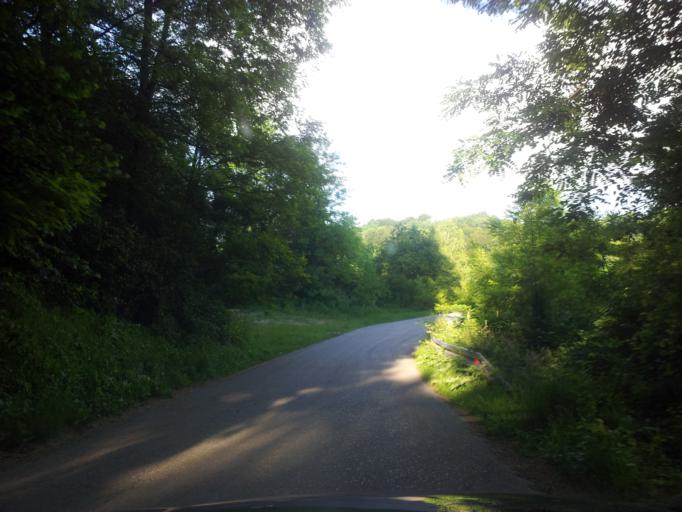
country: HR
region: Karlovacka
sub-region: Grad Karlovac
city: Karlovac
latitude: 45.4732
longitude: 15.4667
